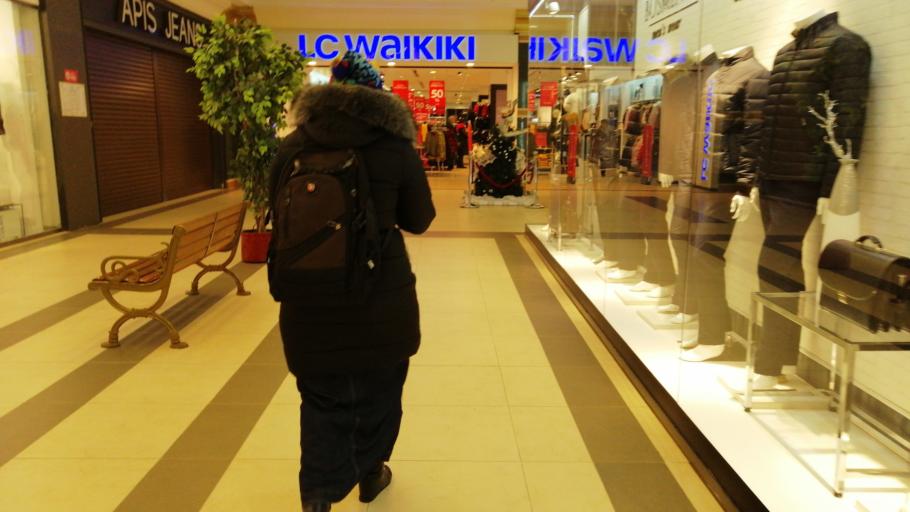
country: KZ
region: Aqtoebe
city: Aqtobe
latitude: 50.2890
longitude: 57.1935
